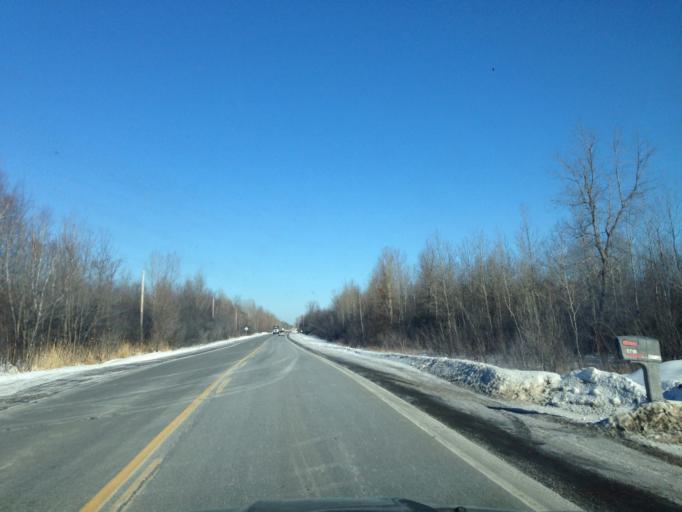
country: CA
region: Ontario
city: Clarence-Rockland
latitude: 45.3293
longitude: -75.4347
